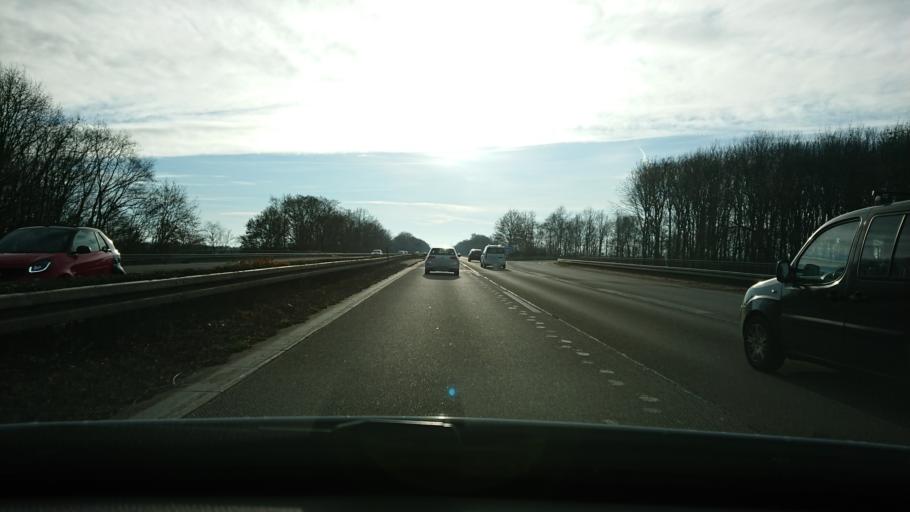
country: DE
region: North Rhine-Westphalia
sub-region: Regierungsbezirk Koln
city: Wahn-Heide
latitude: 50.8446
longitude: 7.0968
